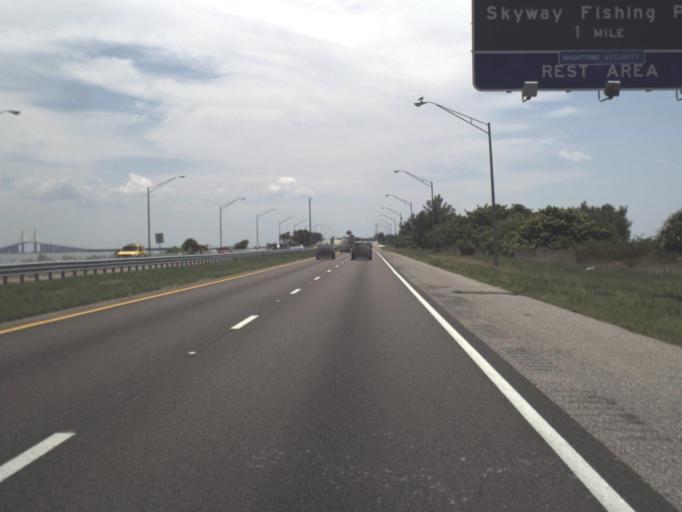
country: US
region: Florida
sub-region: Pinellas County
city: Tierra Verde
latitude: 27.6693
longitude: -82.6778
